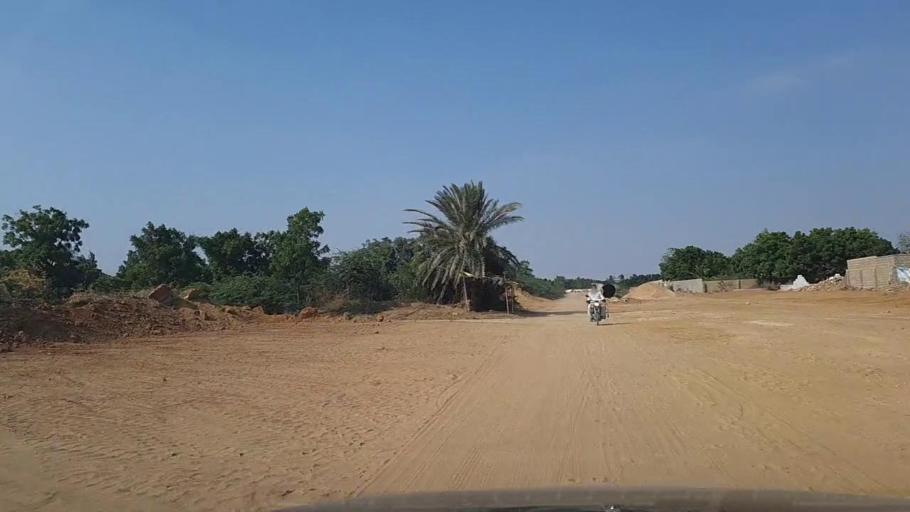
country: PK
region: Sindh
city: Gharo
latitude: 24.7641
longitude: 67.5777
